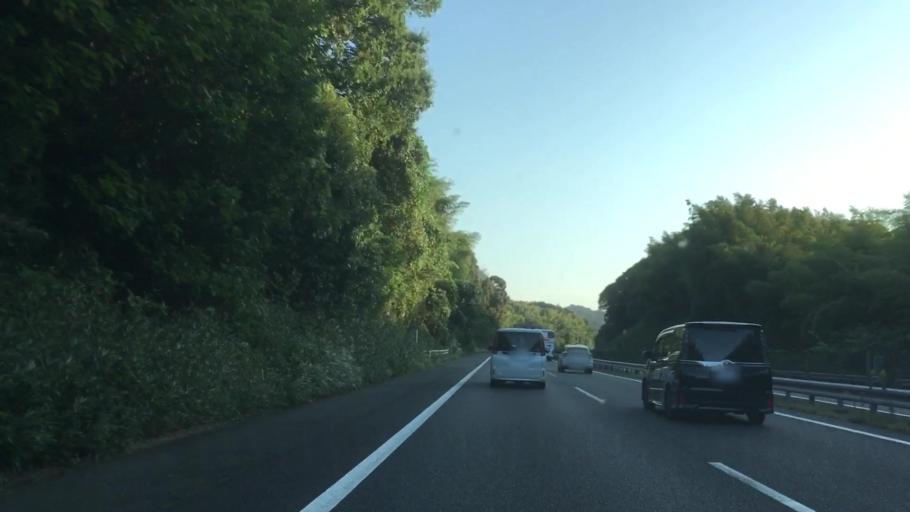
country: JP
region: Yamaguchi
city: Shimonoseki
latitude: 34.0568
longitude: 131.0073
